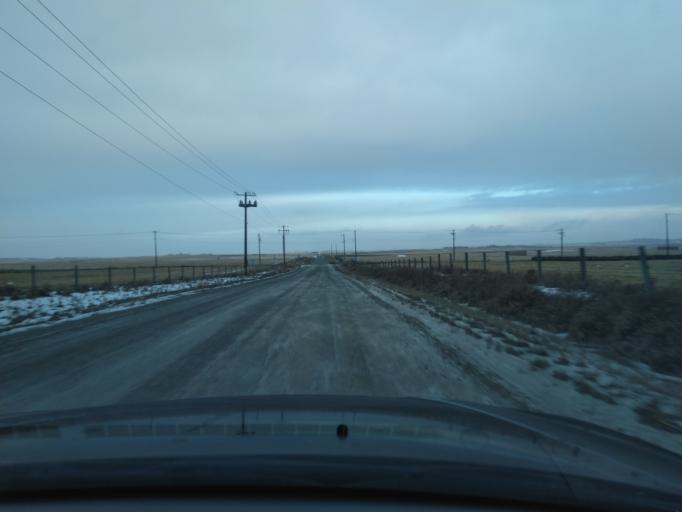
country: CA
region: Alberta
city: Airdrie
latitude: 51.1819
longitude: -114.0248
